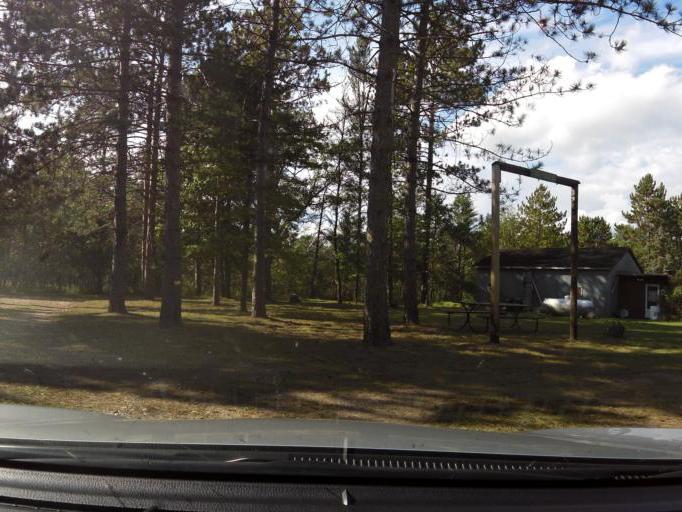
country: US
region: Michigan
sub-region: Roscommon County
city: Roscommon
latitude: 44.5262
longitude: -84.5866
